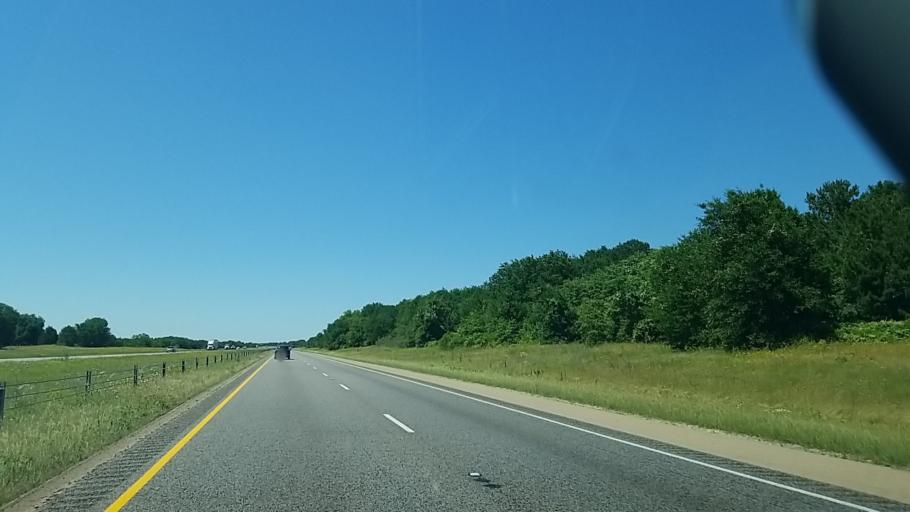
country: US
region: Texas
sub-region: Freestone County
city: Fairfield
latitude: 31.6697
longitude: -96.1630
